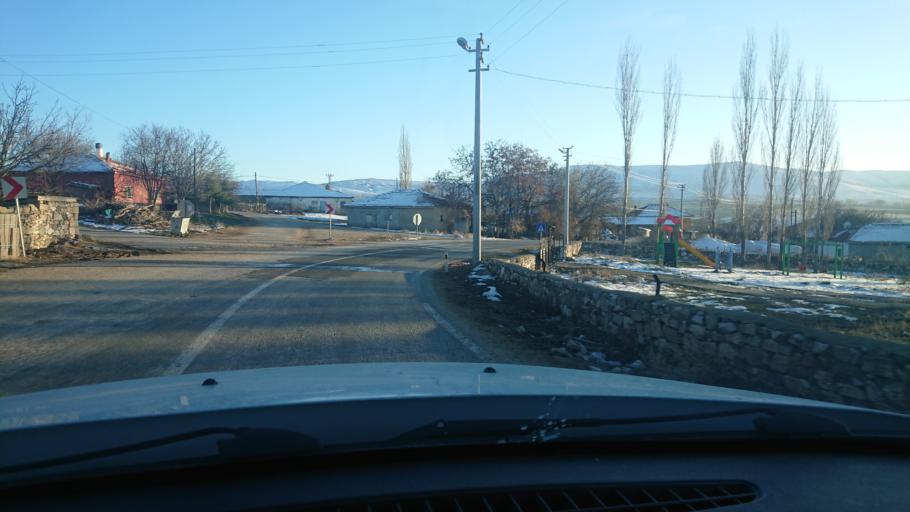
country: TR
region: Aksaray
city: Ortakoy
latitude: 38.7568
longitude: 33.9341
